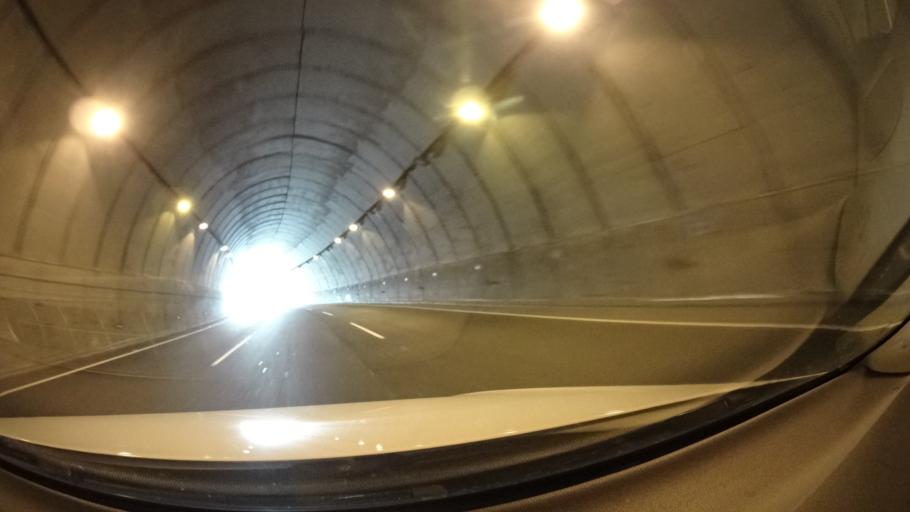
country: ES
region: Canary Islands
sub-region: Provincia de Las Palmas
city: Santa Brigida
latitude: 28.0508
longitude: -15.4635
